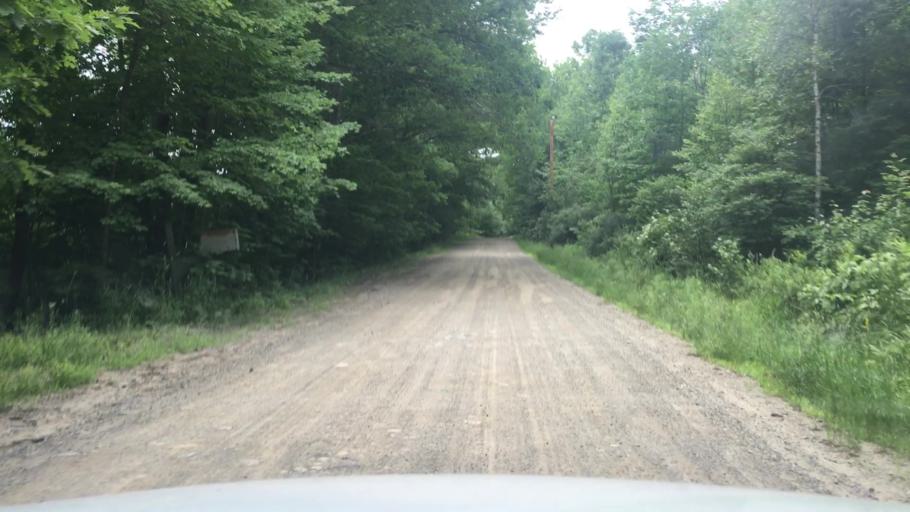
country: US
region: Maine
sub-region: Waldo County
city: Searsmont
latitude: 44.4274
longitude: -69.2562
